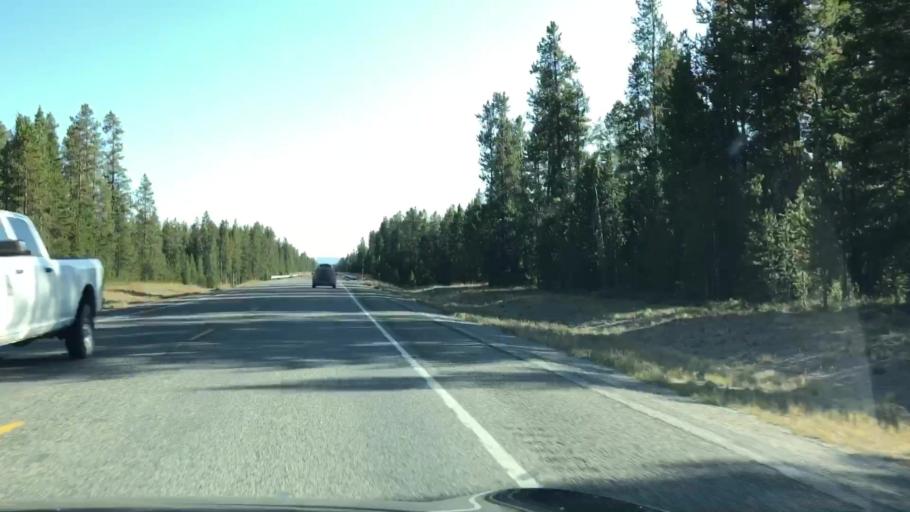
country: US
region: Montana
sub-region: Gallatin County
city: West Yellowstone
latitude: 44.7553
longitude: -111.1133
